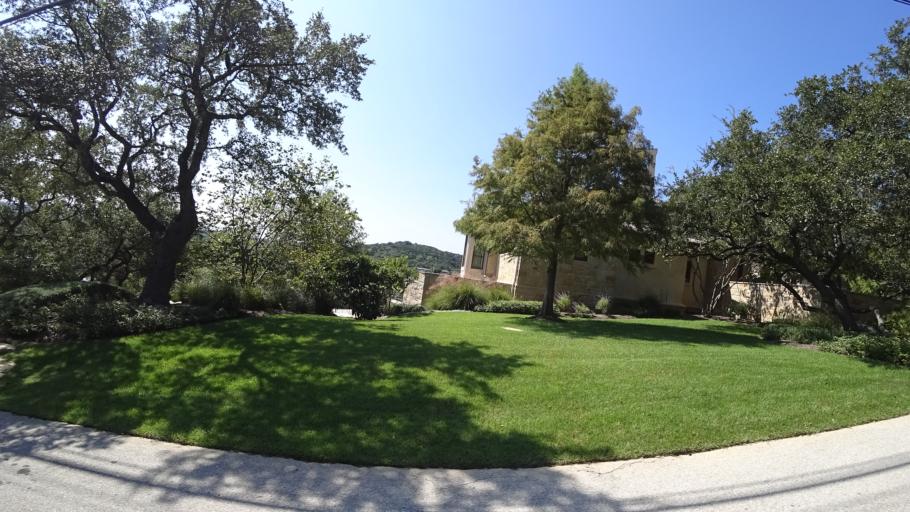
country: US
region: Texas
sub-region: Travis County
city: West Lake Hills
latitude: 30.3043
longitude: -97.7915
